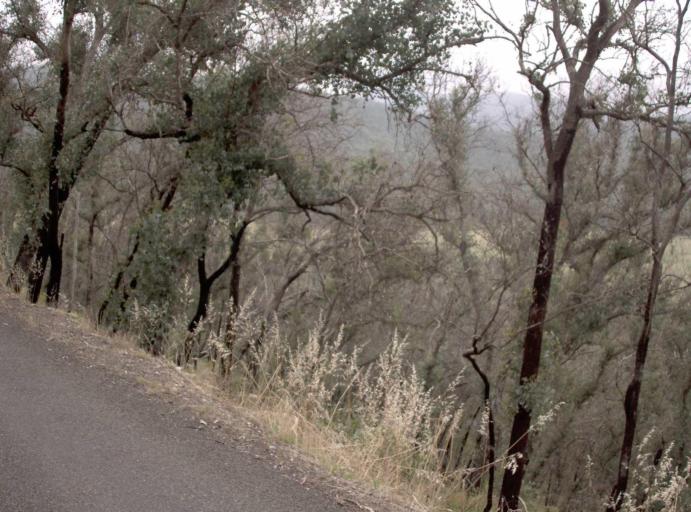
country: AU
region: Victoria
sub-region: Wellington
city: Heyfield
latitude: -37.8177
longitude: 146.6729
